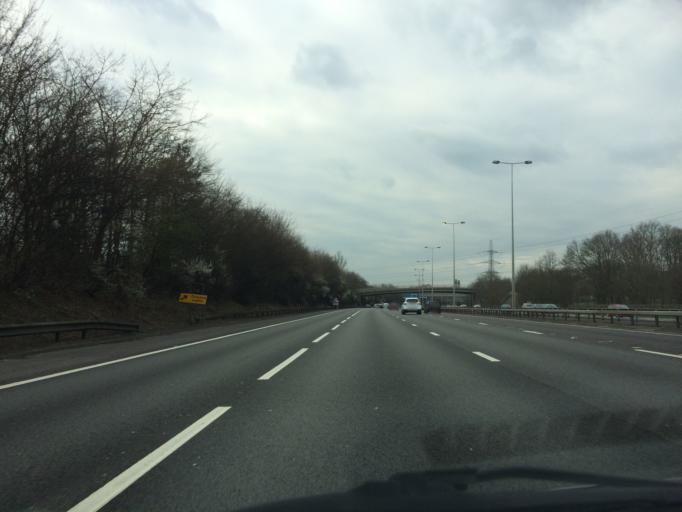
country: GB
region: England
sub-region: Surrey
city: Chertsey
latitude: 51.3882
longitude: -0.5258
